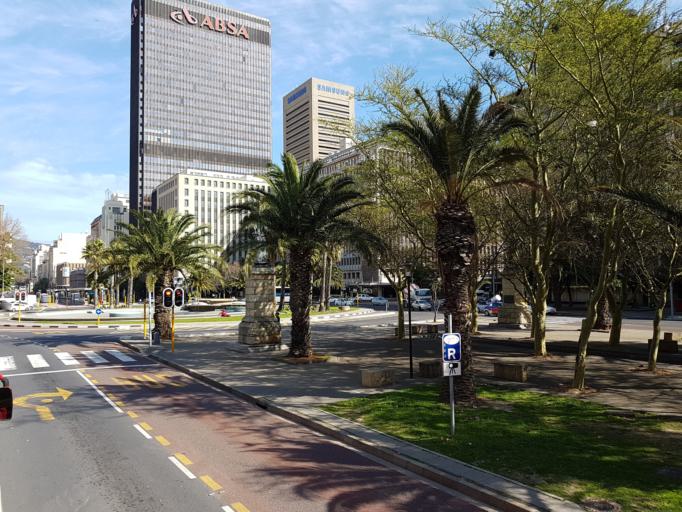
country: ZA
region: Western Cape
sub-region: City of Cape Town
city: Cape Town
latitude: -33.9194
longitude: 18.4263
